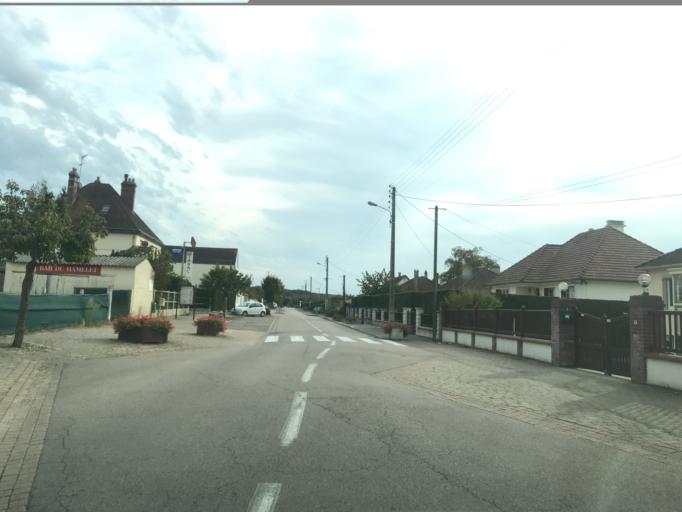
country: FR
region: Haute-Normandie
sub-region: Departement de l'Eure
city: Louviers
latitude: 49.2008
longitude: 1.1857
